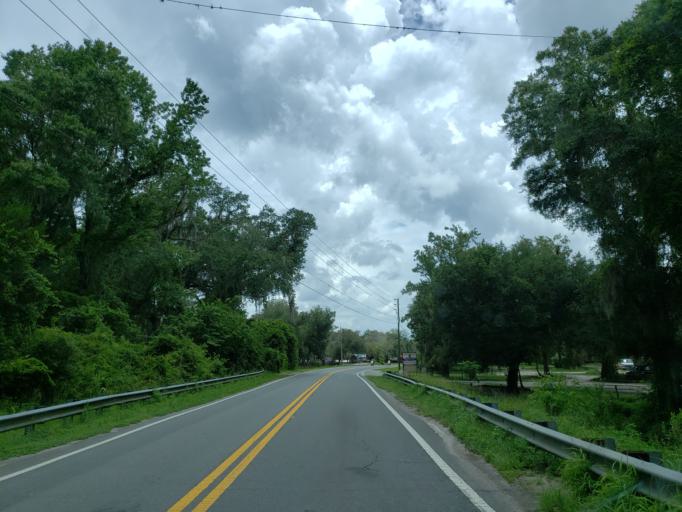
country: US
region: Florida
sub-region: Citrus County
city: Floral City
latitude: 28.6447
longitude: -82.2577
